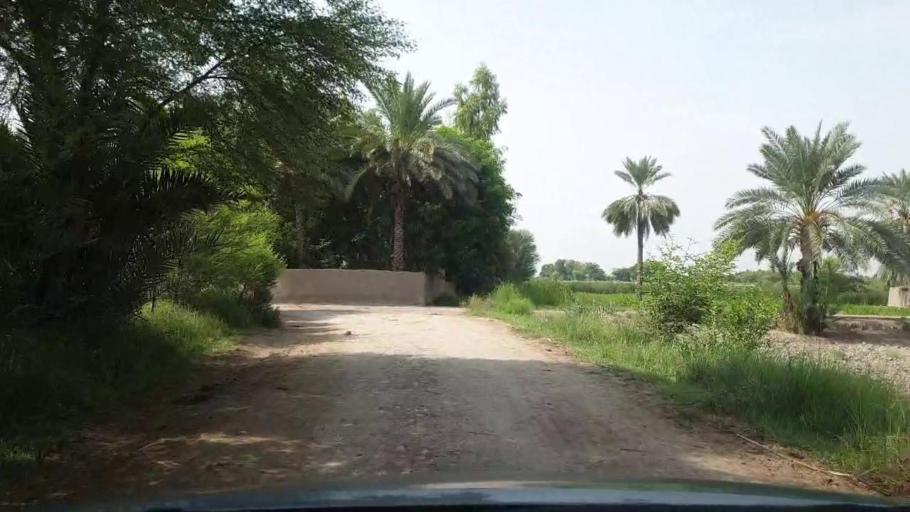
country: PK
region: Sindh
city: Rohri
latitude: 27.6536
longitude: 69.0102
